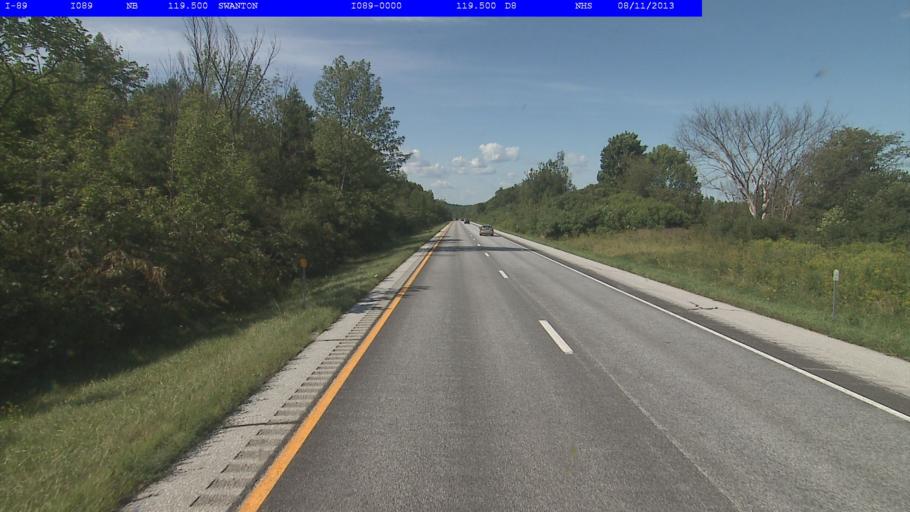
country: US
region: Vermont
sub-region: Franklin County
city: Saint Albans
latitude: 44.8699
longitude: -73.0818
